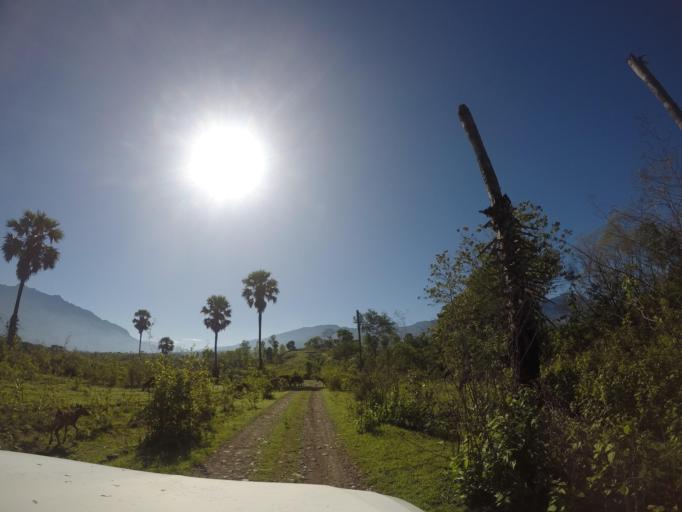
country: TL
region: Bobonaro
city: Maliana
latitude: -8.9984
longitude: 125.1930
